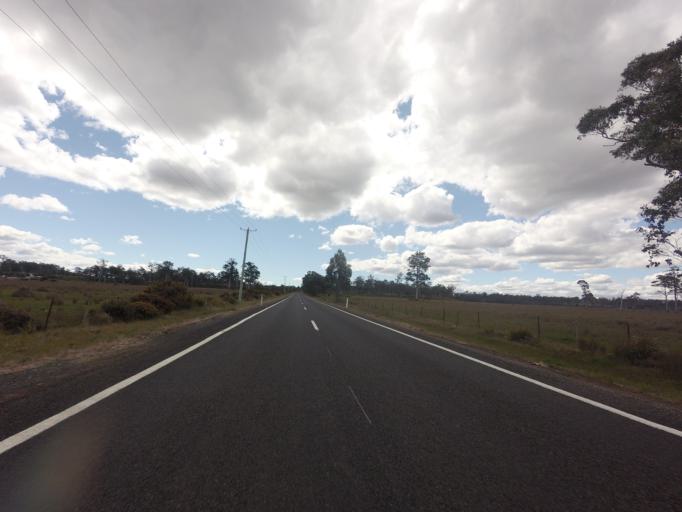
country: AU
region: Tasmania
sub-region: Northern Midlands
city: Evandale
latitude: -41.9854
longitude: 147.6696
